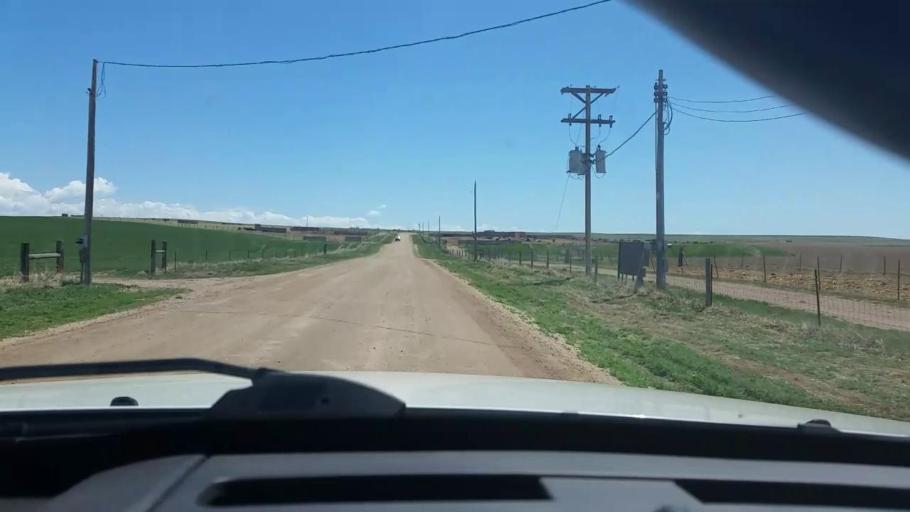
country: US
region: Colorado
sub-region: Larimer County
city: Wellington
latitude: 40.7982
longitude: -105.0449
